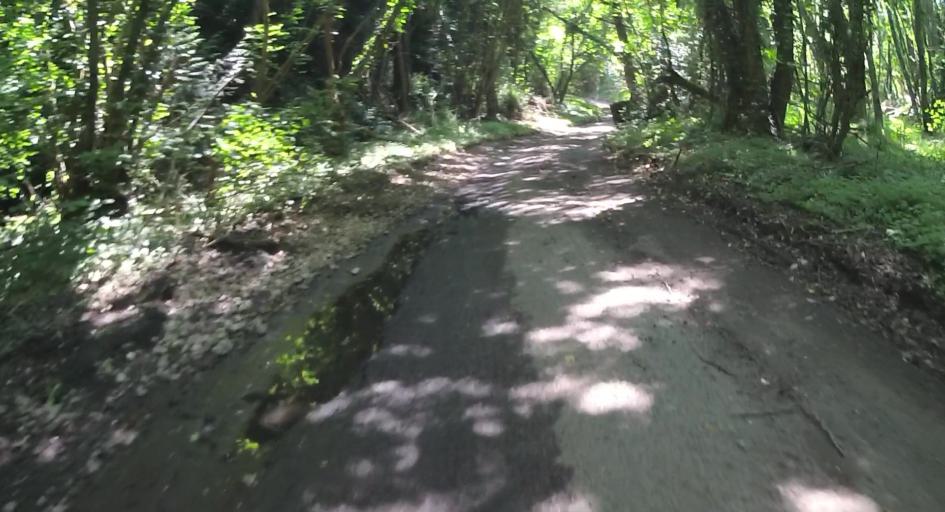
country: GB
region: England
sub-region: Hampshire
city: Kingsclere
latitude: 51.3548
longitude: -1.2739
